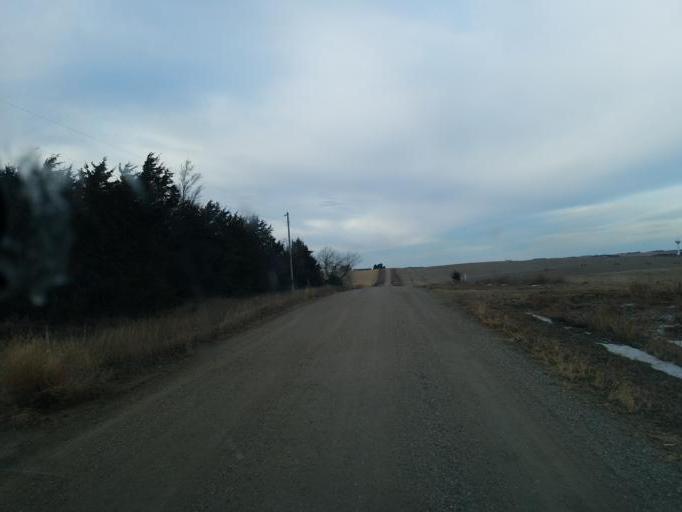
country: US
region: Nebraska
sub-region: Knox County
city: Bloomfield
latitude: 42.5833
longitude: -97.6293
